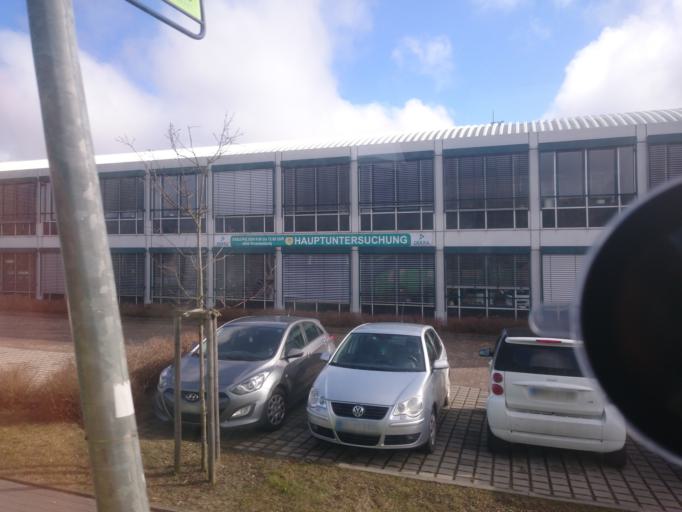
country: DE
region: Mecklenburg-Vorpommern
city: Papendorf
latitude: 54.0613
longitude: 12.1176
